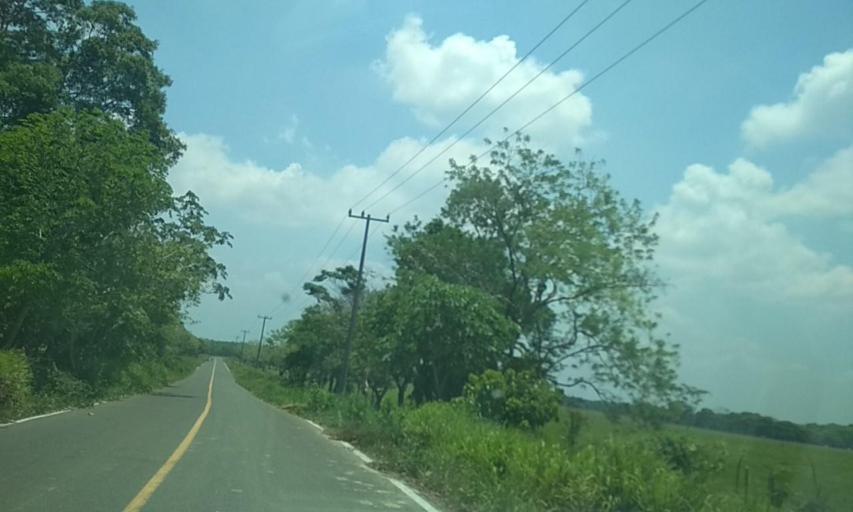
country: MX
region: Tabasco
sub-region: Huimanguillo
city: Francisco Rueda
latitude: 17.7584
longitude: -94.0557
